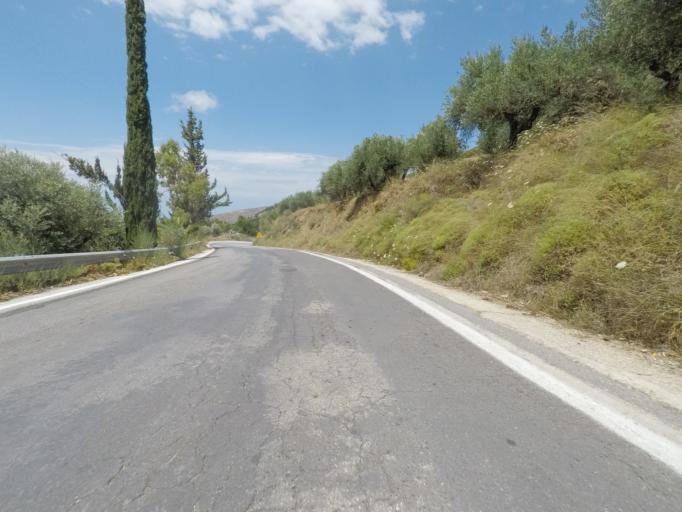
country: GR
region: Crete
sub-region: Nomos Irakleiou
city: Mokhos
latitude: 35.2180
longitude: 25.4601
